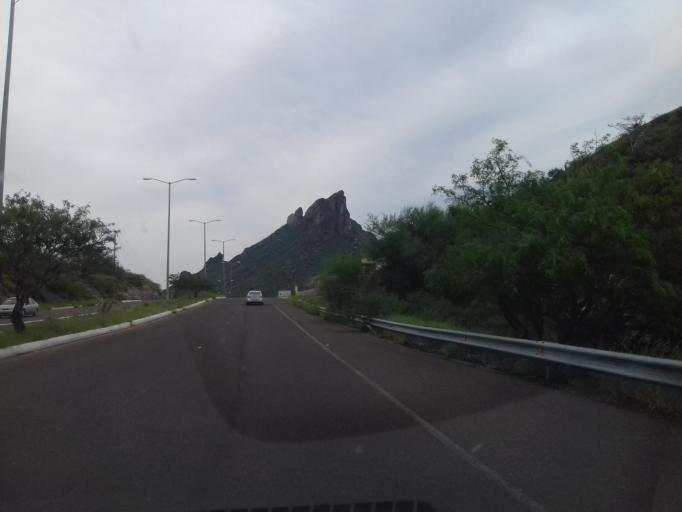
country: MX
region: Sonora
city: Heroica Guaymas
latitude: 27.9563
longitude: -111.0927
